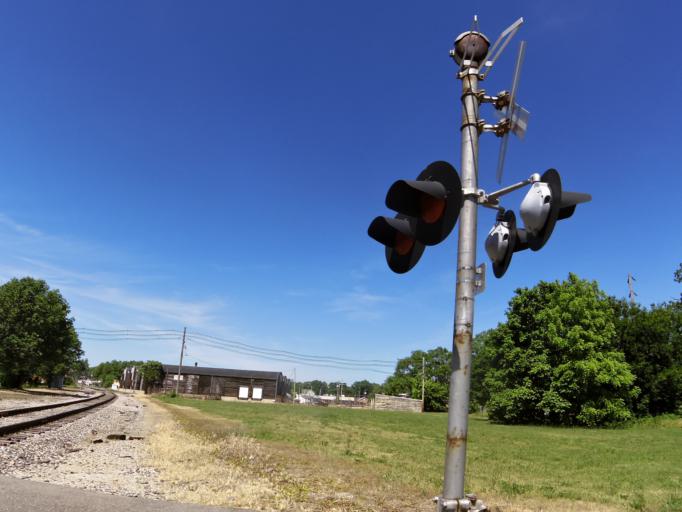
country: US
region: Illinois
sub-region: Vermilion County
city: Danville
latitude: 40.1353
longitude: -87.6316
